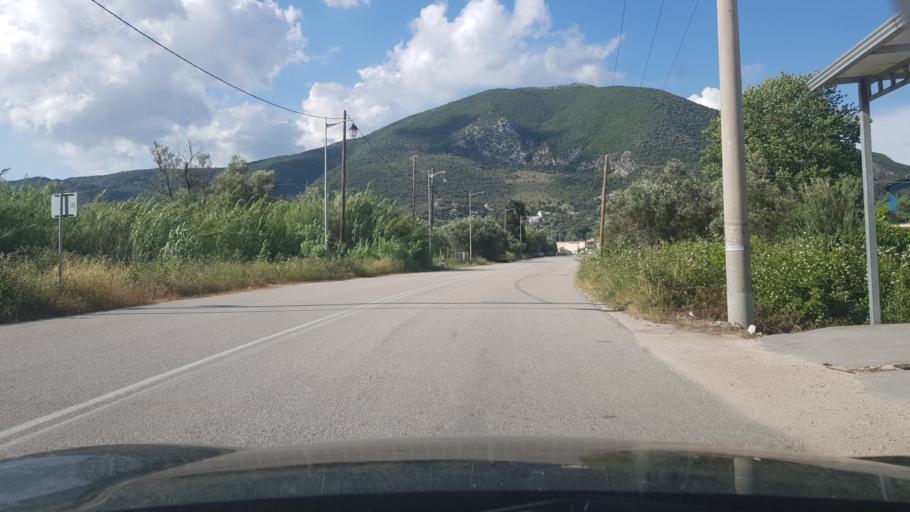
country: GR
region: Ionian Islands
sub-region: Lefkada
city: Nidri
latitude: 38.7059
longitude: 20.7038
